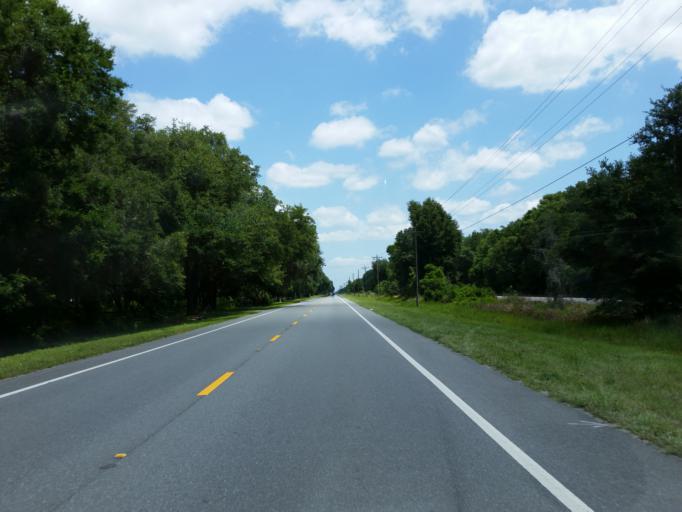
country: US
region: Florida
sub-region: Sumter County
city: Bushnell
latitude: 28.5995
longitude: -82.1436
